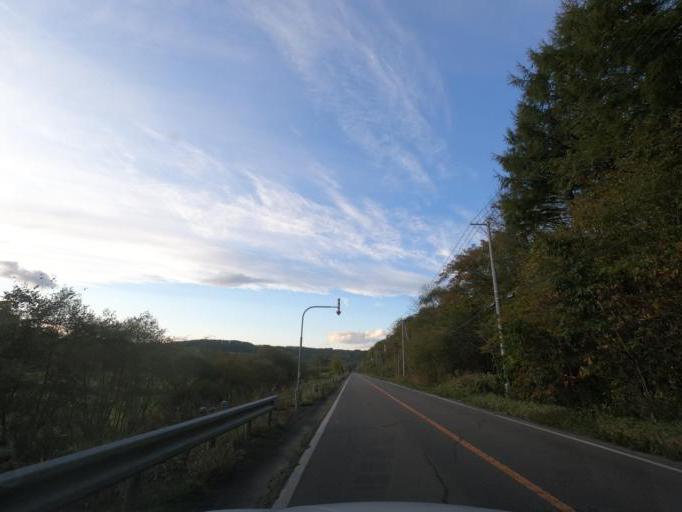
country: JP
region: Hokkaido
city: Obihiro
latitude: 42.5834
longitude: 143.3089
